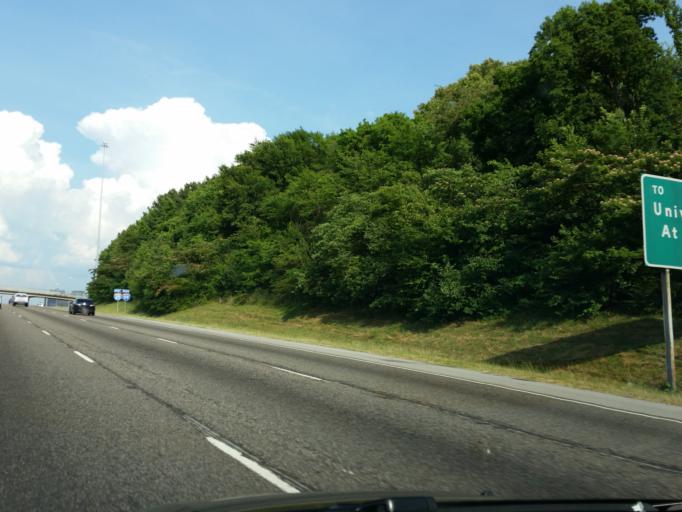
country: US
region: Alabama
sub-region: Jefferson County
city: Birmingham
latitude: 33.5208
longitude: -86.8403
